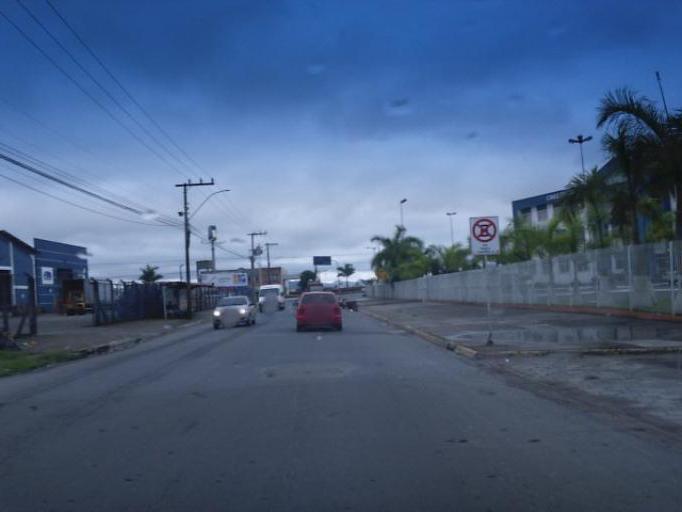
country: BR
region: Santa Catarina
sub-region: Itajai
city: Itajai
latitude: -26.9146
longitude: -48.7008
